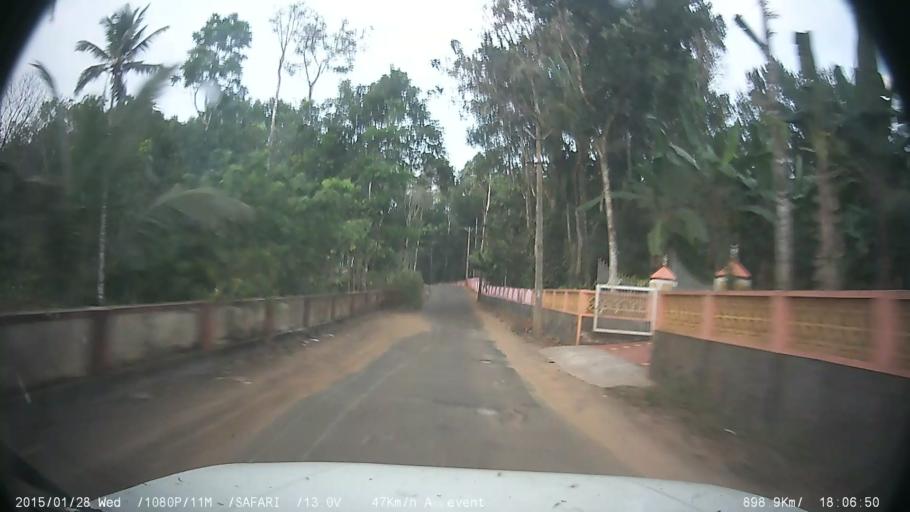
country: IN
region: Kerala
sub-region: Kottayam
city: Palackattumala
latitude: 9.7311
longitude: 76.5764
